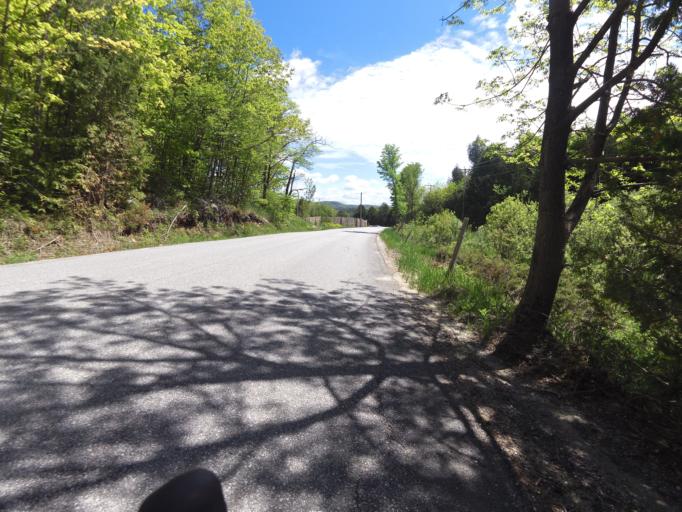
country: CA
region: Quebec
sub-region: Outaouais
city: Wakefield
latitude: 45.6756
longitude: -75.9527
